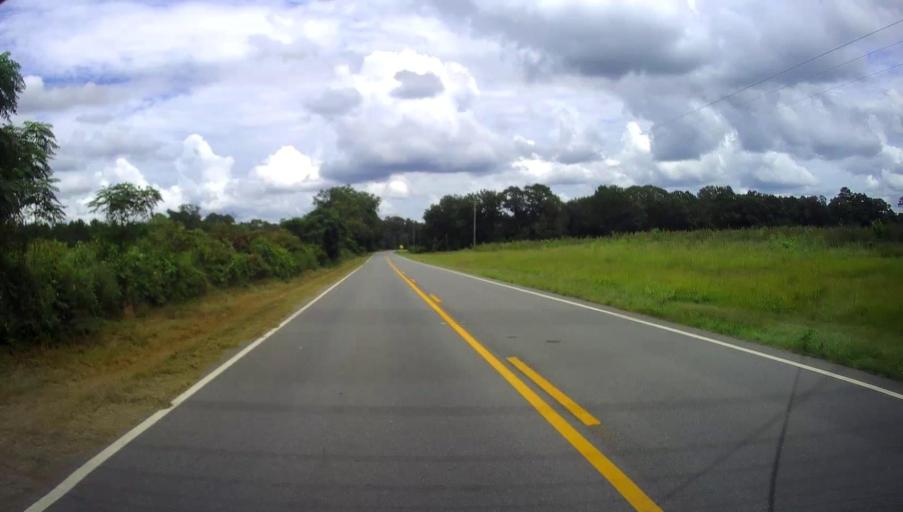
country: US
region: Georgia
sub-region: Macon County
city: Oglethorpe
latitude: 32.2832
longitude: -84.1671
